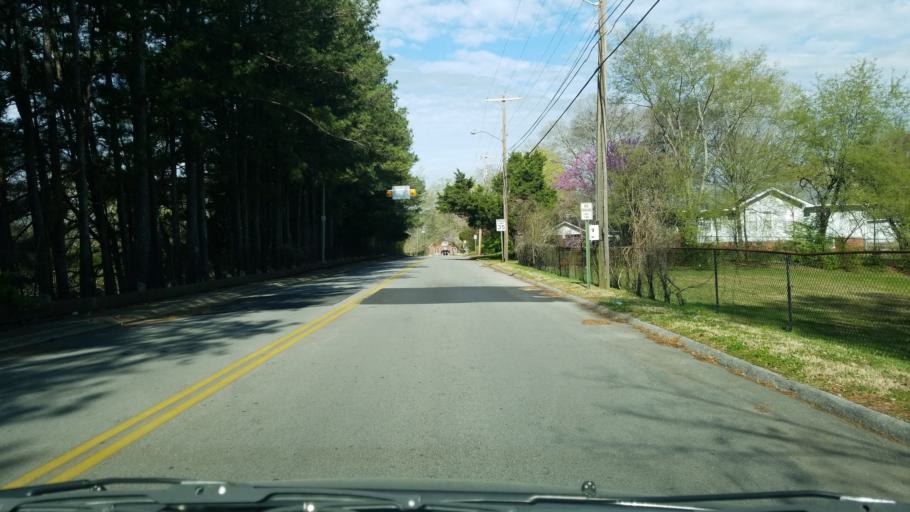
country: US
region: Tennessee
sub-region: Hamilton County
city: Harrison
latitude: 35.0620
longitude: -85.1547
